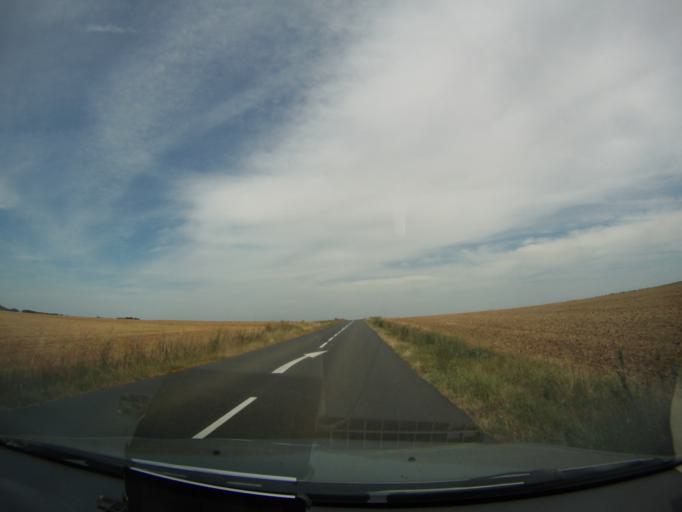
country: FR
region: Poitou-Charentes
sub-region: Departement de la Vienne
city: Moncontour
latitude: 46.8091
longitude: -0.0234
